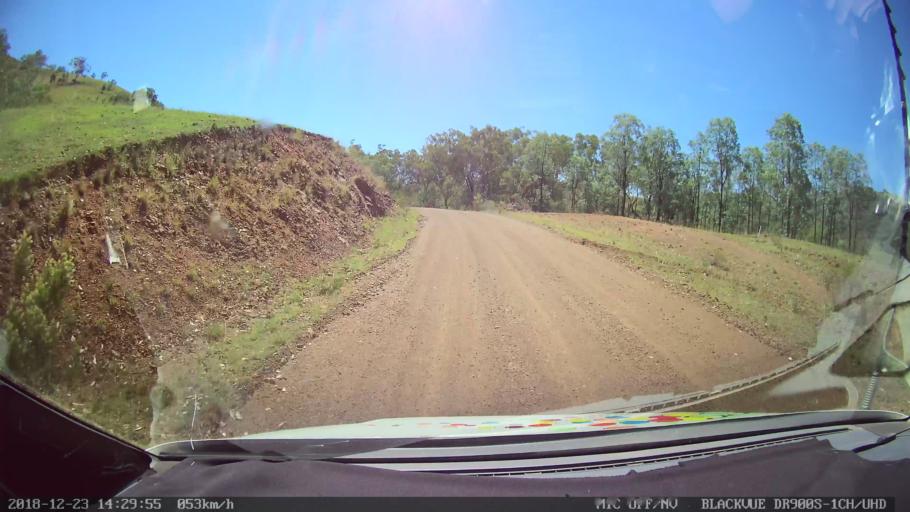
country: AU
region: New South Wales
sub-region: Tamworth Municipality
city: Manilla
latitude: -30.6055
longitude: 150.9356
